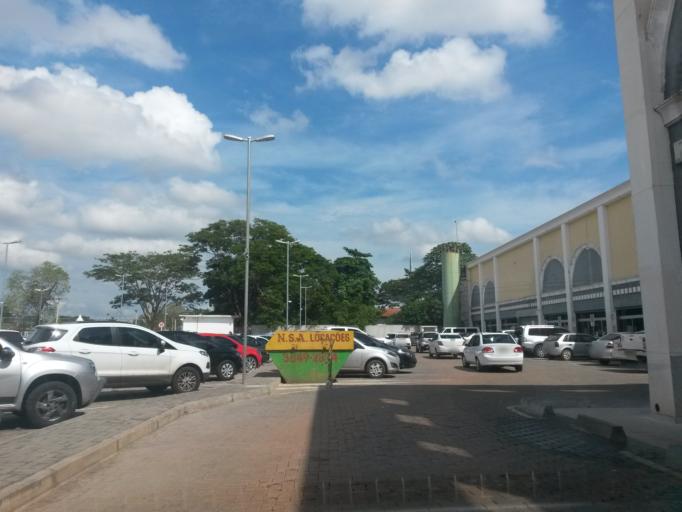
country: BR
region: Mato Grosso
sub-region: Cuiaba
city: Cuiaba
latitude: -15.6135
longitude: -56.1014
